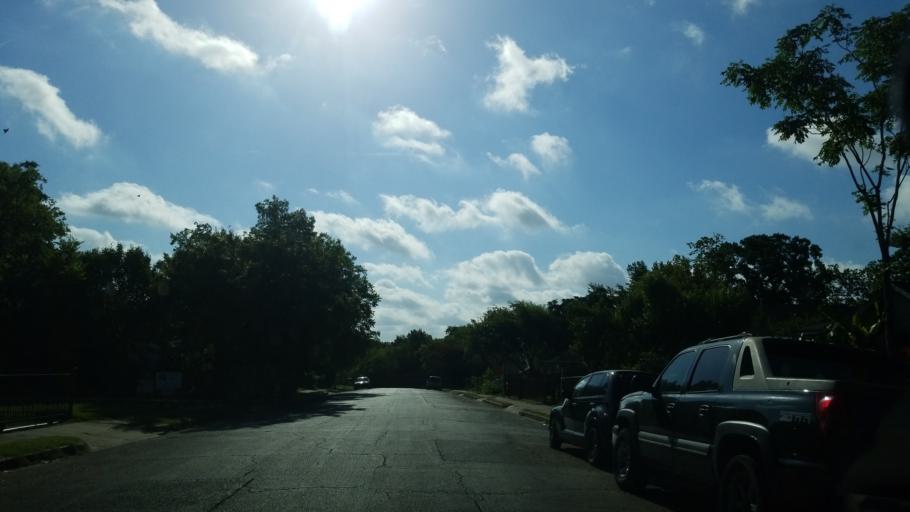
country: US
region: Texas
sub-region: Dallas County
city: Dallas
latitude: 32.7276
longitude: -96.8029
